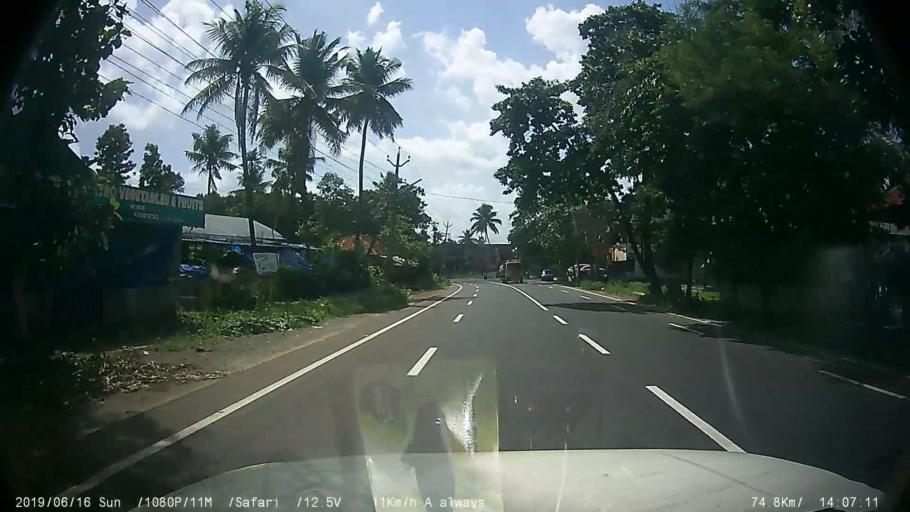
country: IN
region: Kerala
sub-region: Ernakulam
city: Muvattupula
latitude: 10.0467
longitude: 76.5332
